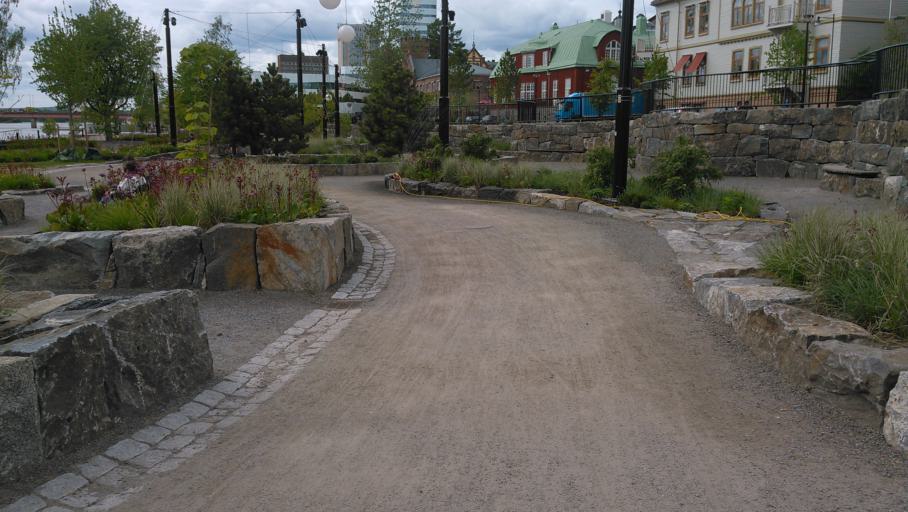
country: SE
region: Vaesterbotten
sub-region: Umea Kommun
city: Umea
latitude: 63.8231
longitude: 20.2658
